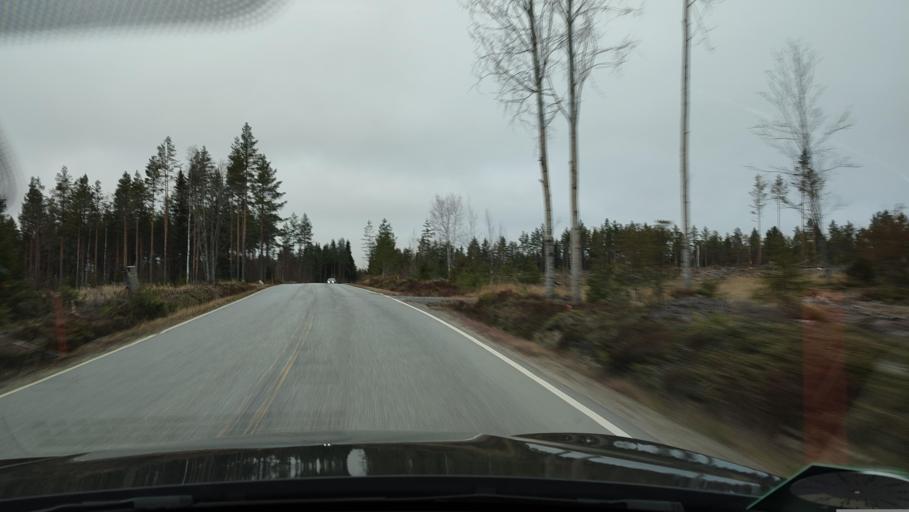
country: FI
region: Southern Ostrobothnia
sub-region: Suupohja
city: Karijoki
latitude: 62.2520
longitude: 21.7510
